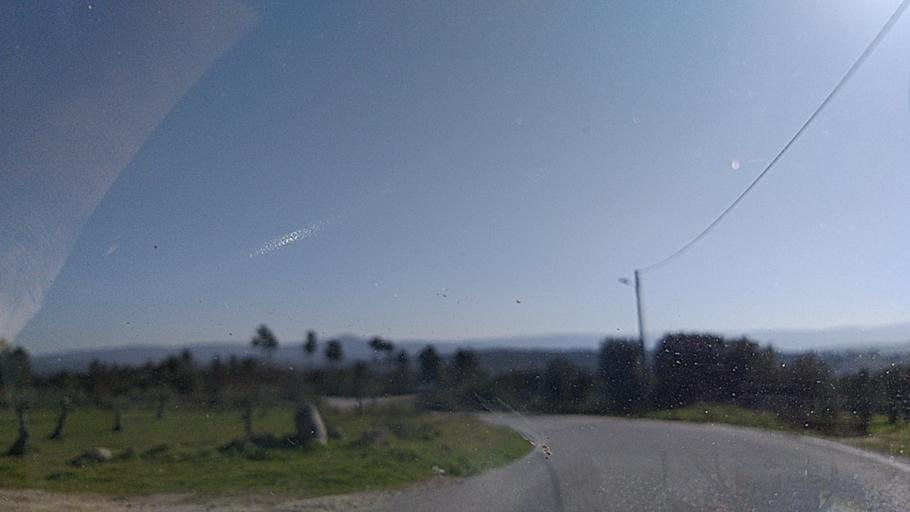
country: PT
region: Guarda
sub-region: Celorico da Beira
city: Celorico da Beira
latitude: 40.6710
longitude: -7.3941
